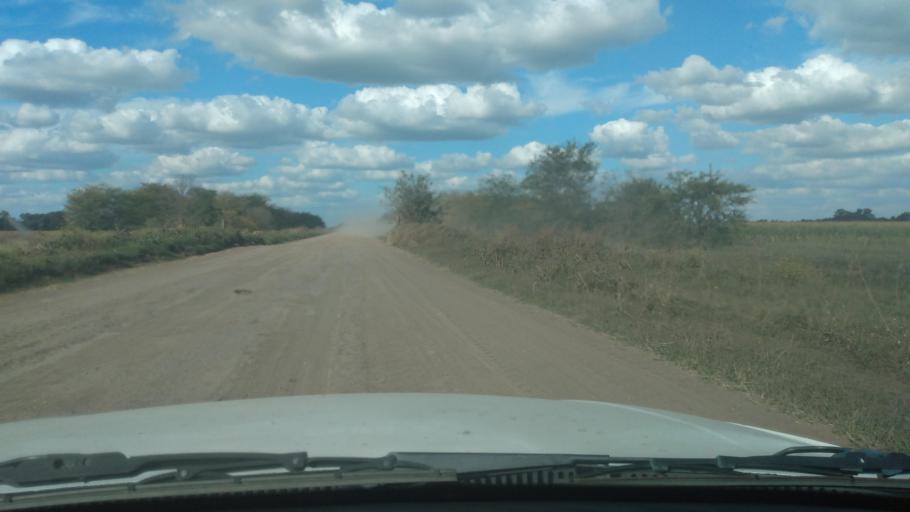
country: AR
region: Buenos Aires
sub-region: Partido de Navarro
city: Navarro
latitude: -35.0124
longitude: -59.4783
